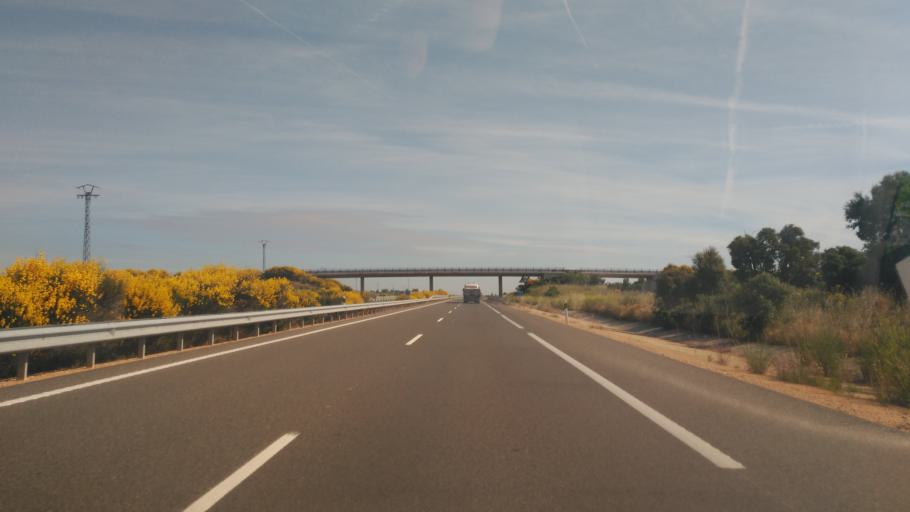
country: ES
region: Castille and Leon
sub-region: Provincia de Salamanca
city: Topas
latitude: 41.1596
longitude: -5.6956
